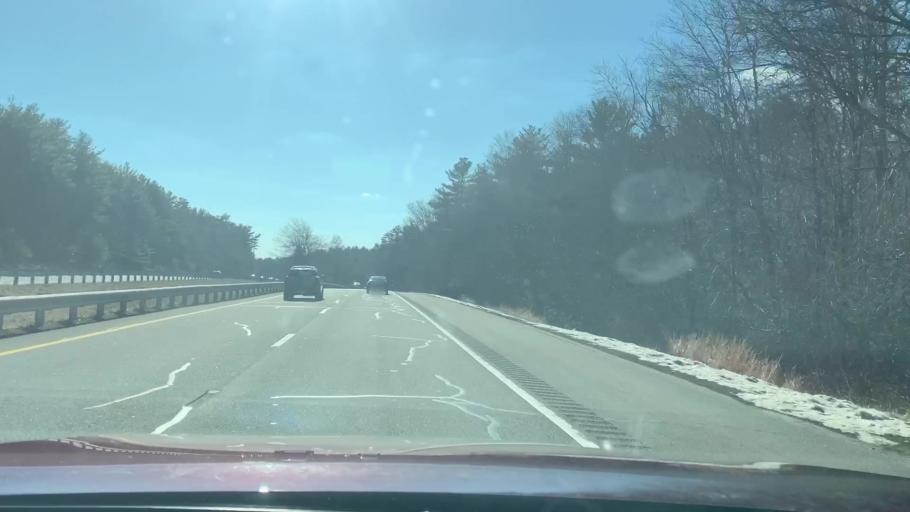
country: US
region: Massachusetts
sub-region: Essex County
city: Essex
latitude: 42.6021
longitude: -70.7458
